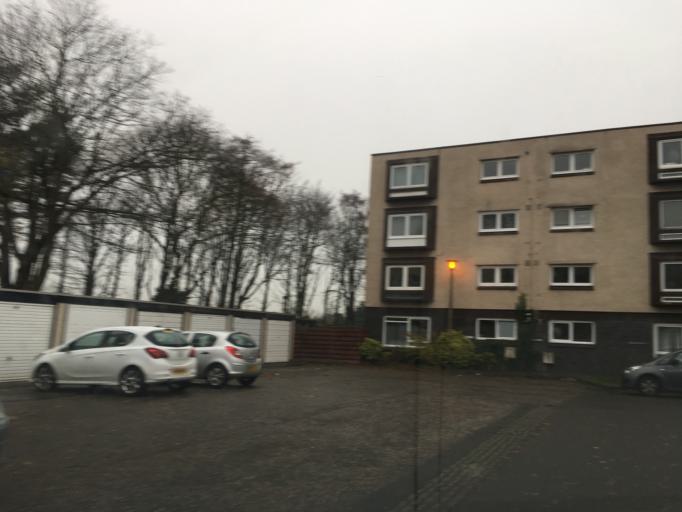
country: GB
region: Scotland
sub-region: Edinburgh
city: Currie
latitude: 55.9579
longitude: -3.3068
